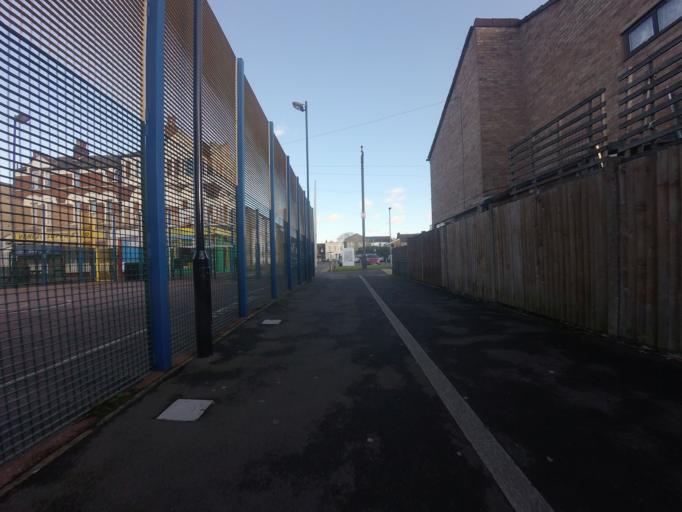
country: GB
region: England
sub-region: Greater London
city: East Ham
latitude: 51.5498
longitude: 0.0111
